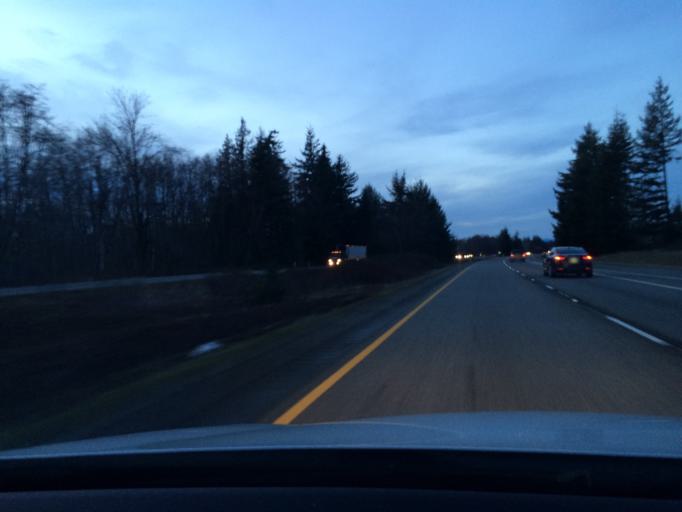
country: US
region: Washington
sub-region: Whatcom County
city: Ferndale
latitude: 48.9102
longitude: -122.6250
